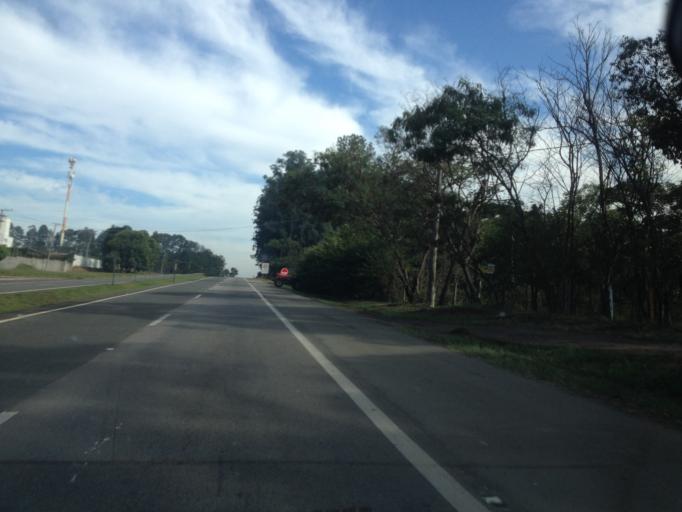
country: BR
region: Sao Paulo
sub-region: Itu
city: Itu
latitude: -23.2543
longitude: -47.3567
